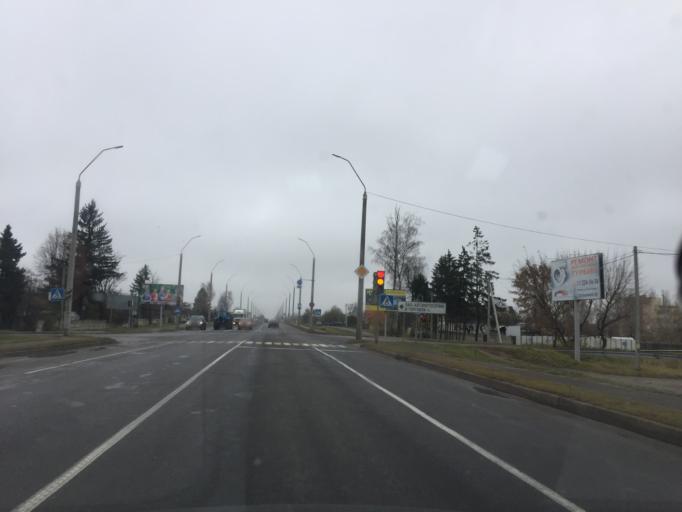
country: BY
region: Mogilev
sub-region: Mahilyowski Rayon
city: Veyno
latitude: 53.8534
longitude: 30.3590
